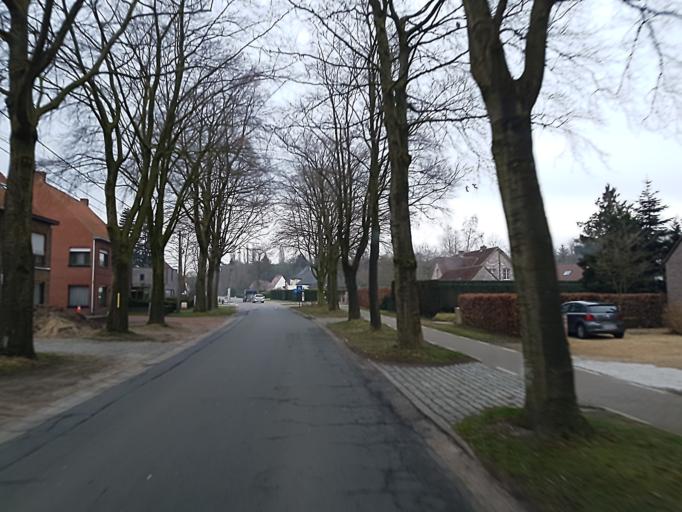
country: BE
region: Flanders
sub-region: Provincie Oost-Vlaanderen
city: Kaprijke
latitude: 51.1827
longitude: 3.6241
